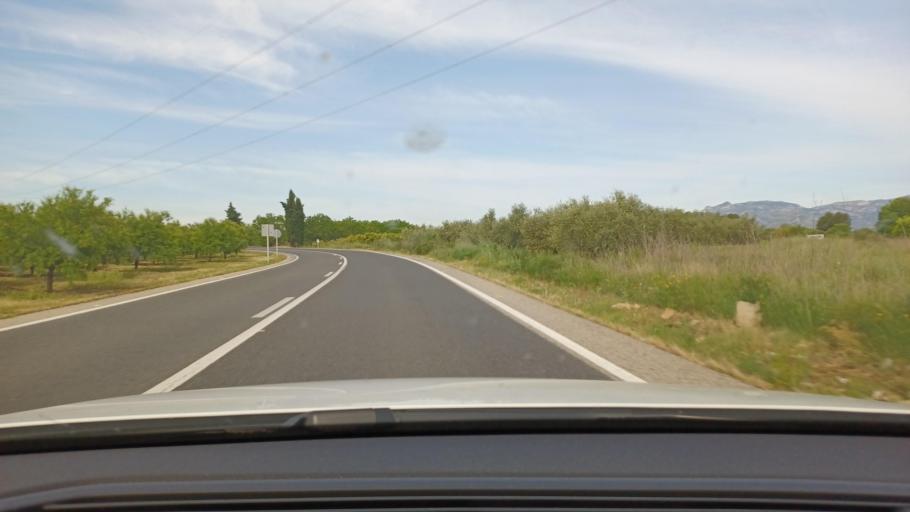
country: ES
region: Catalonia
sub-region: Provincia de Tarragona
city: Santa Barbara
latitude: 40.6774
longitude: 0.4522
